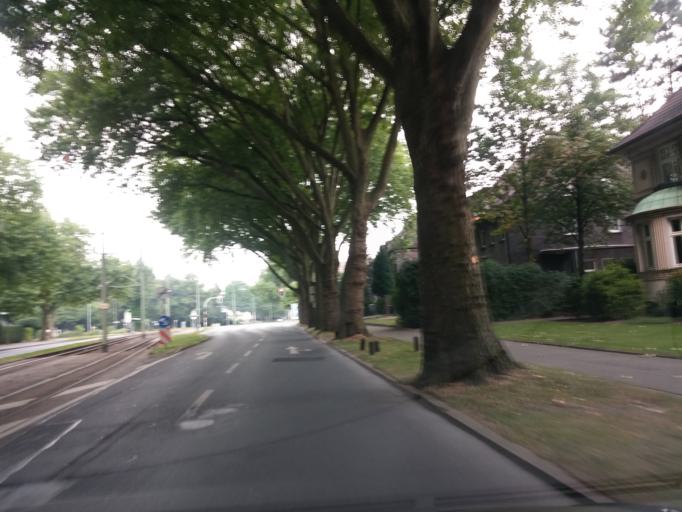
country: DE
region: North Rhine-Westphalia
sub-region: Regierungsbezirk Munster
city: Gladbeck
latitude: 51.5751
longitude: 7.0642
